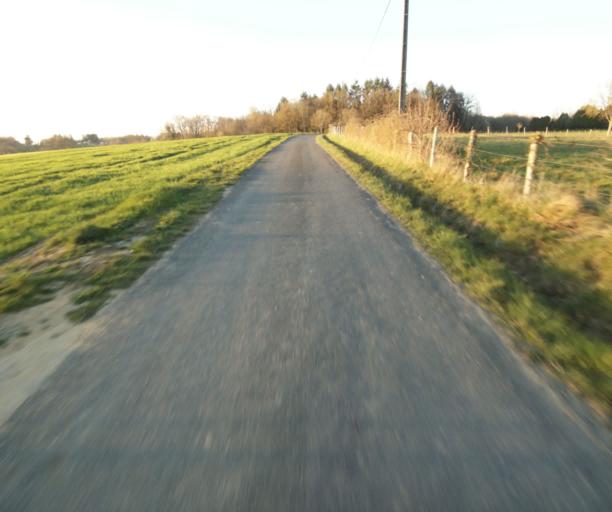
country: FR
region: Limousin
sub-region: Departement de la Correze
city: Saint-Mexant
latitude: 45.3078
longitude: 1.6538
